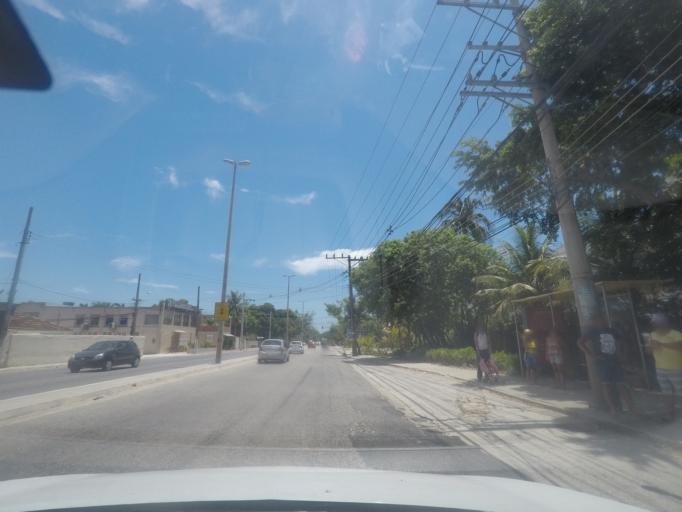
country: BR
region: Rio de Janeiro
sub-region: Itaguai
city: Itaguai
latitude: -22.8991
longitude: -43.6793
